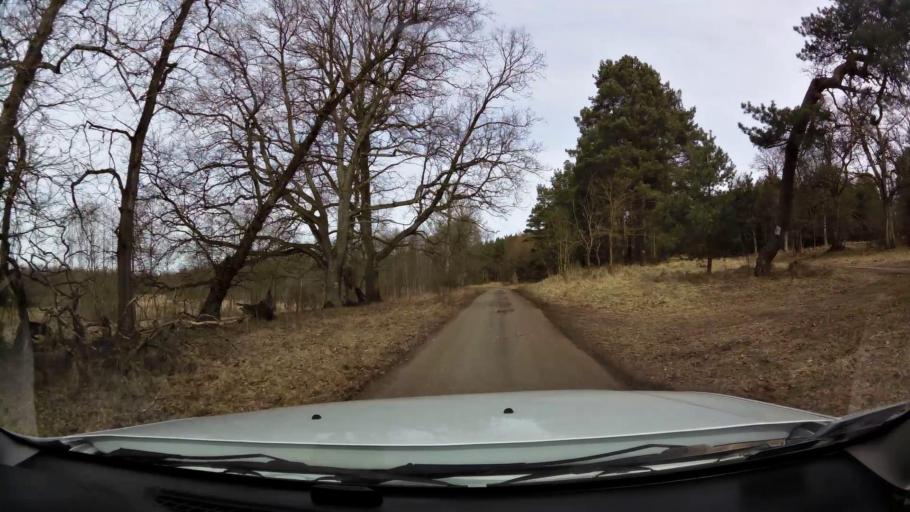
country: PL
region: West Pomeranian Voivodeship
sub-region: Powiat drawski
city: Drawsko Pomorskie
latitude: 53.4745
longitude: 15.6996
